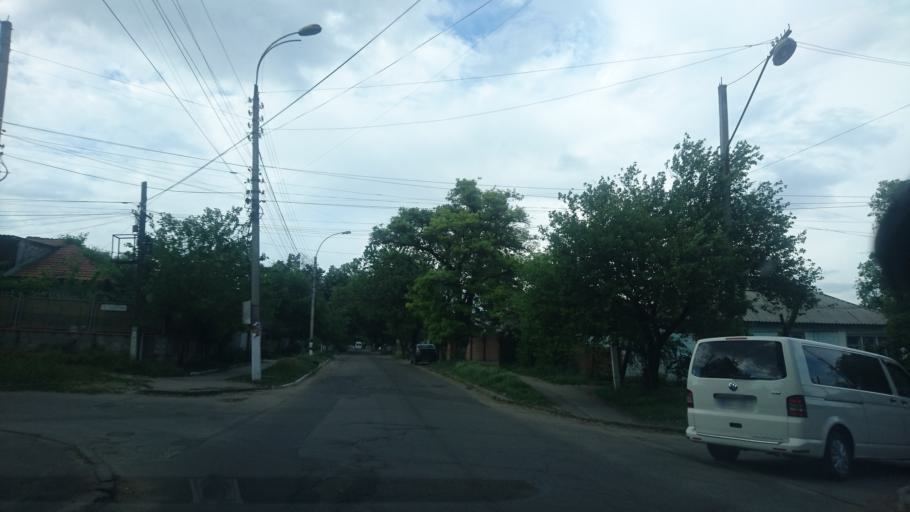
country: MD
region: Chisinau
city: Chisinau
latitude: 47.0474
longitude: 28.8469
